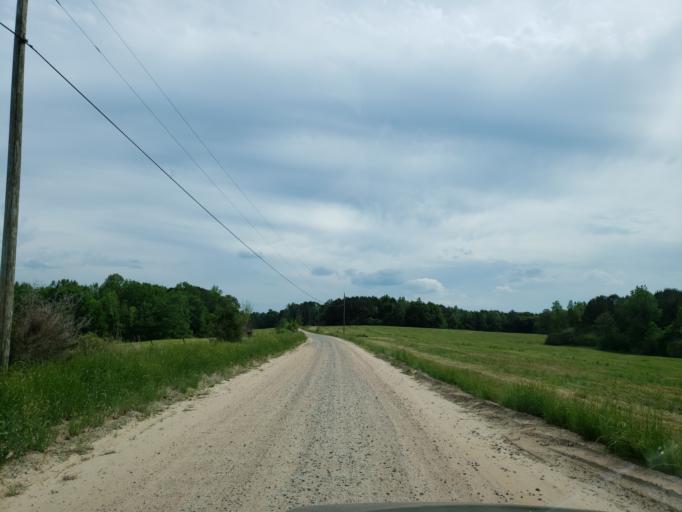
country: US
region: Georgia
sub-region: Monroe County
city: Forsyth
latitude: 32.9768
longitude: -83.9136
